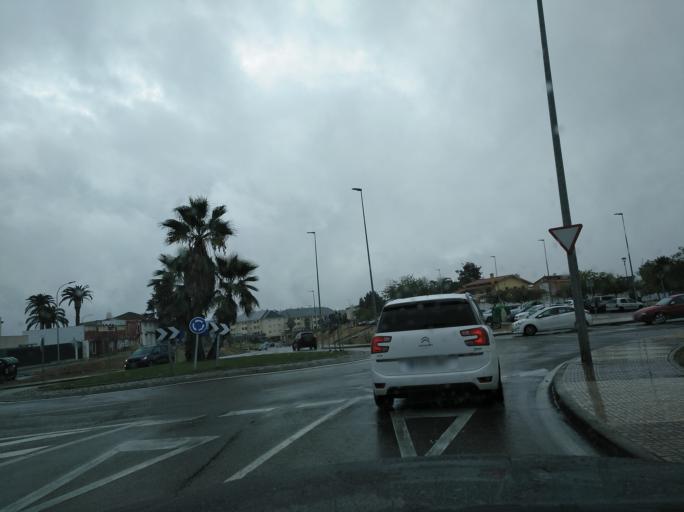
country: ES
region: Extremadura
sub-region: Provincia de Badajoz
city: Badajoz
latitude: 38.8854
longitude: -6.9901
